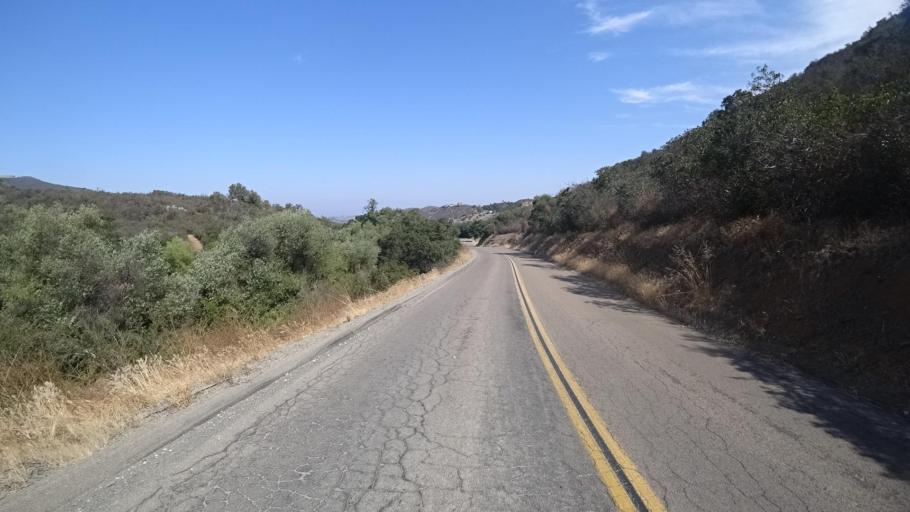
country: US
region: California
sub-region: San Diego County
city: Hidden Meadows
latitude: 33.2212
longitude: -117.1751
